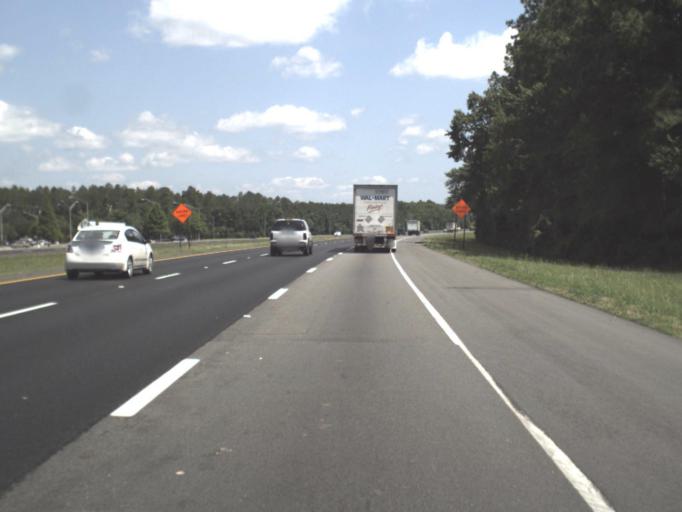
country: US
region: Florida
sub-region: Nassau County
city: Yulee
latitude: 30.6946
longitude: -81.6761
